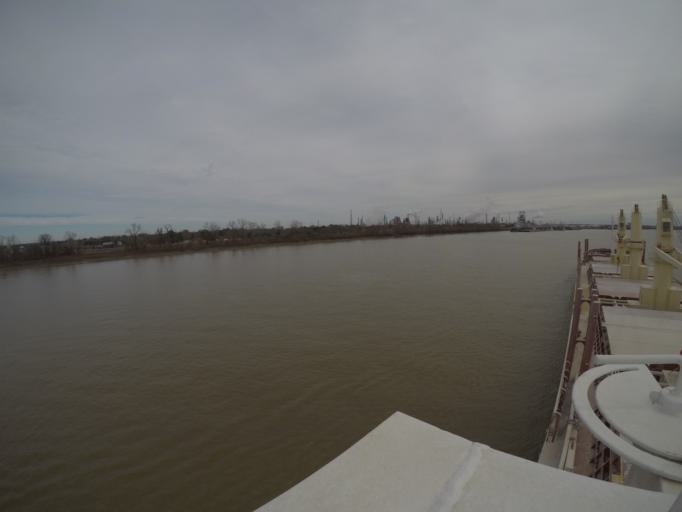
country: US
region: Louisiana
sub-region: Saint Charles Parish
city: Norco
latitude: 29.9945
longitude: -90.4211
